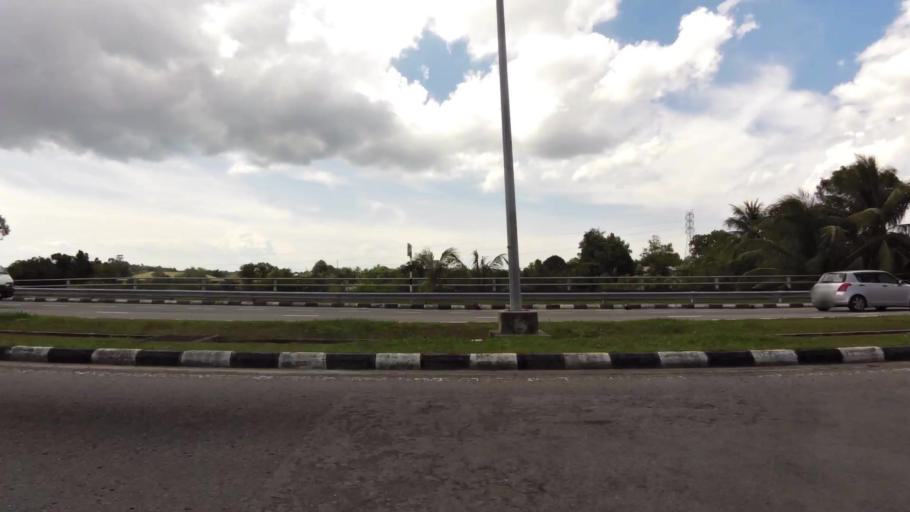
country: BN
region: Brunei and Muara
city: Bandar Seri Begawan
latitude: 4.9474
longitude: 114.9594
